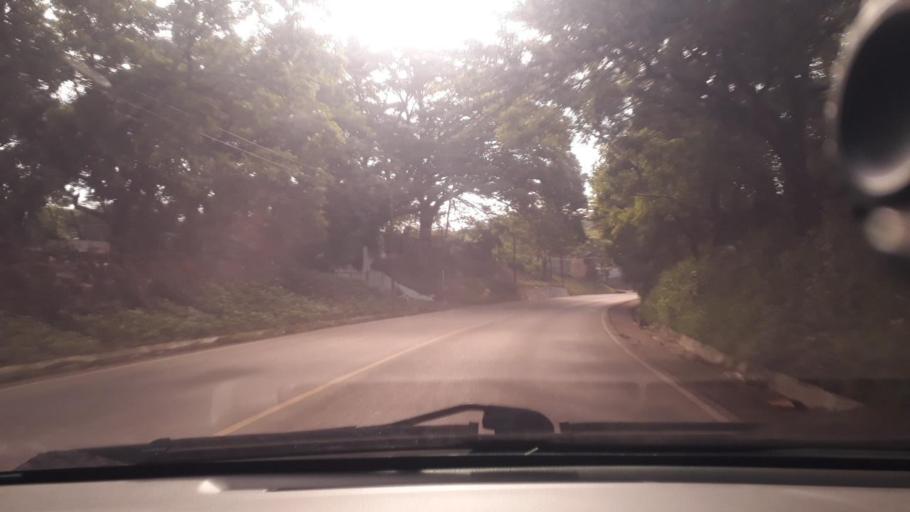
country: GT
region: Jutiapa
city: Jutiapa
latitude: 14.3017
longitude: -89.8918
